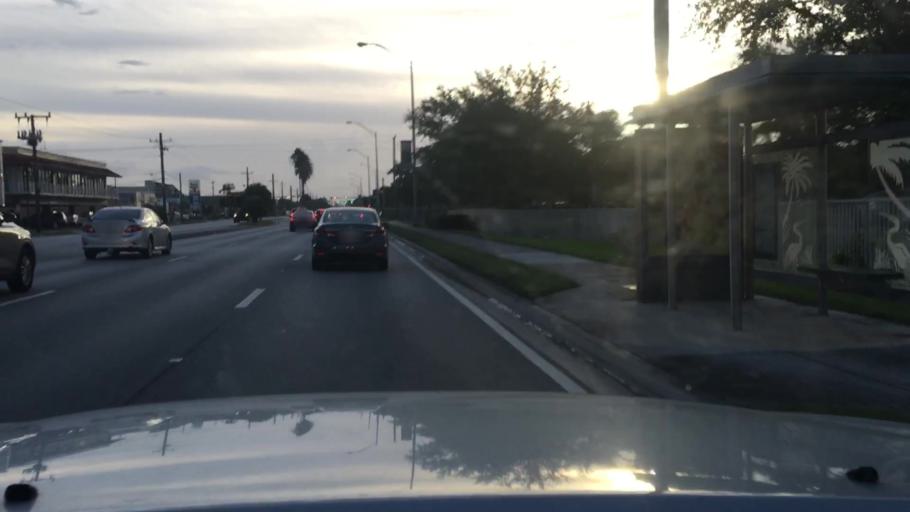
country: US
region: Florida
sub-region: Miami-Dade County
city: Sweetwater
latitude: 25.7688
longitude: -80.3639
